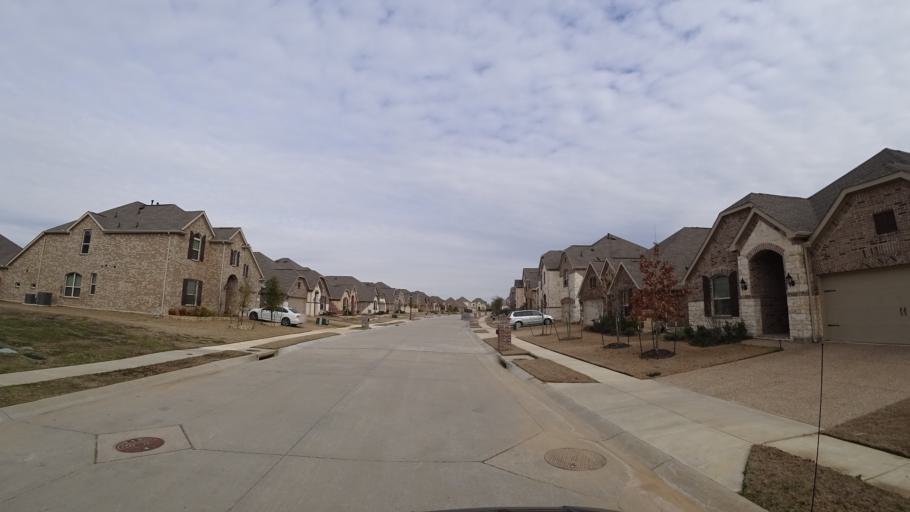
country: US
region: Texas
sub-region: Denton County
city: The Colony
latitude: 33.0483
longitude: -96.9164
